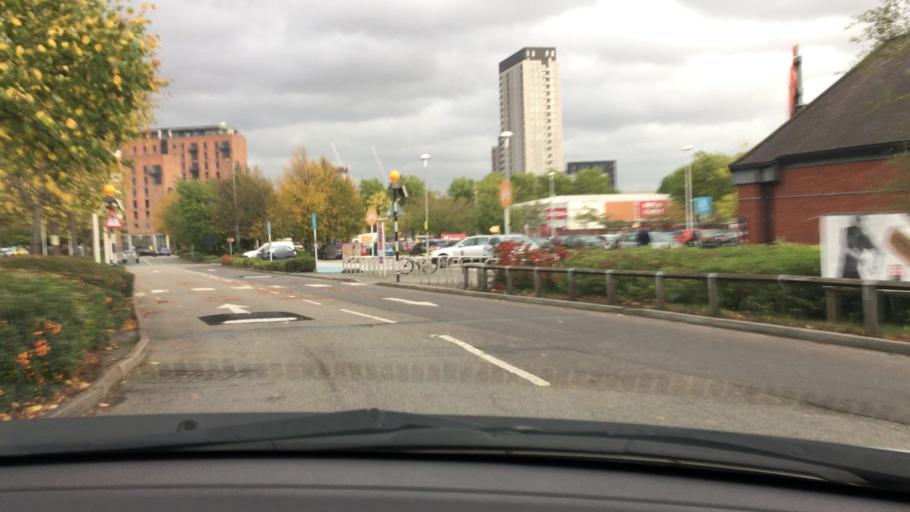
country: GB
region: England
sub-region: Manchester
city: Hulme
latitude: 53.4775
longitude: -2.2675
